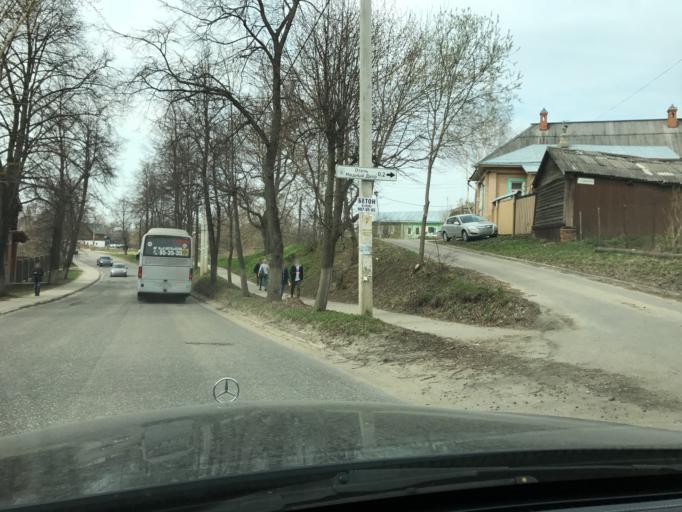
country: RU
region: Vladimir
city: Suzdal'
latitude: 56.4238
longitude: 40.4399
